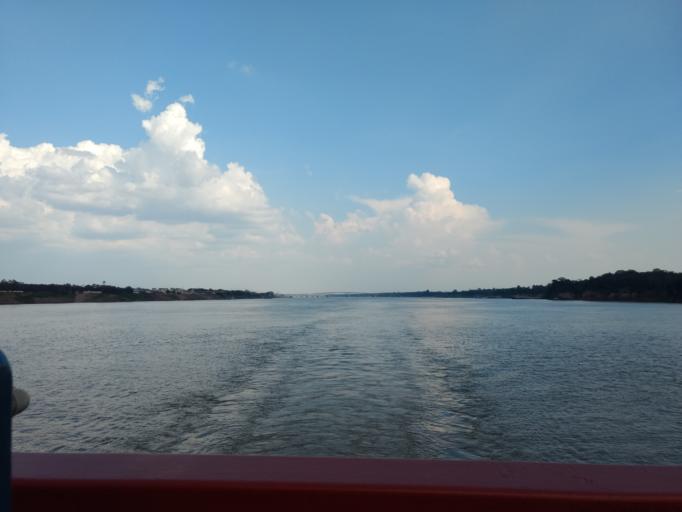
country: BR
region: Rondonia
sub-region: Porto Velho
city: Porto Velho
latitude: -8.6971
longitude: -63.9223
